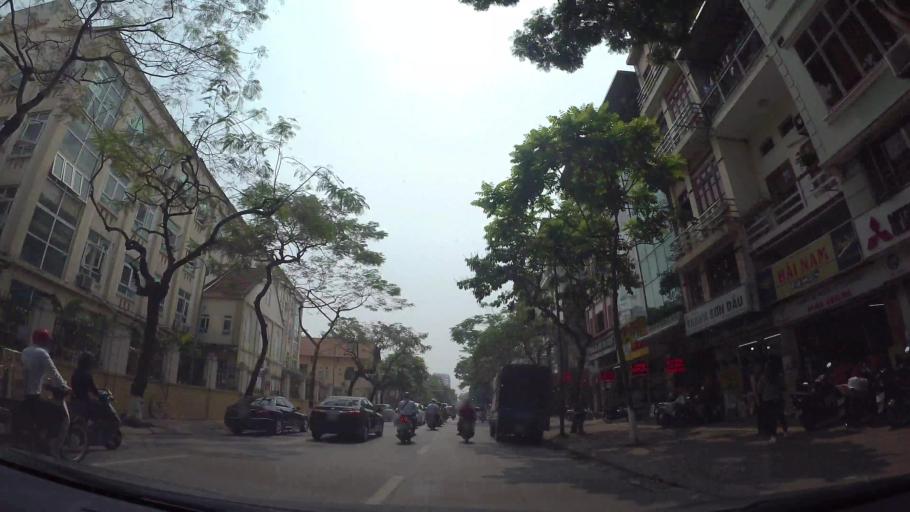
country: VN
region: Ha Noi
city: Hanoi
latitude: 21.0308
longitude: 105.8346
